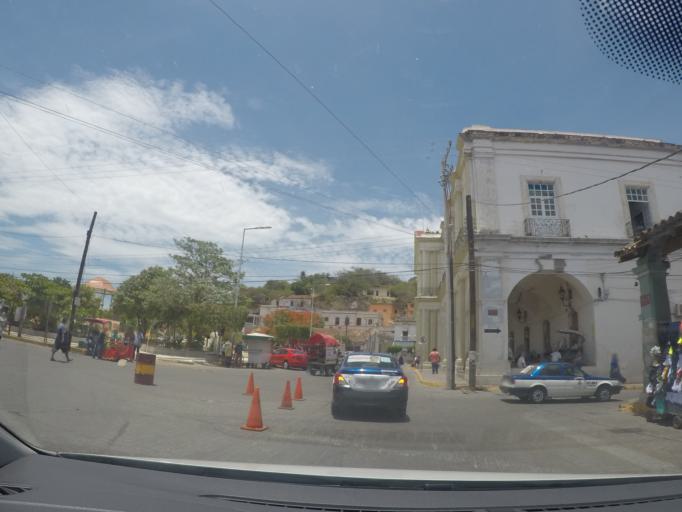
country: MX
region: Oaxaca
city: San Blas Atempa
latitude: 16.3322
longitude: -95.2324
